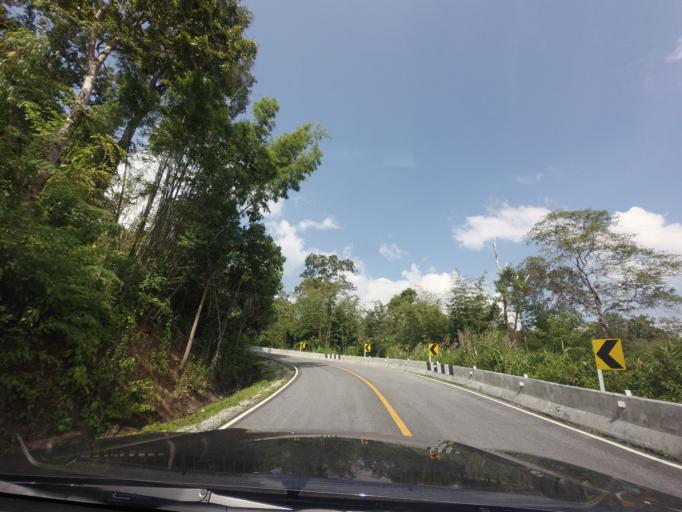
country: TH
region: Uttaradit
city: Ban Khok
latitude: 18.2212
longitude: 101.0349
